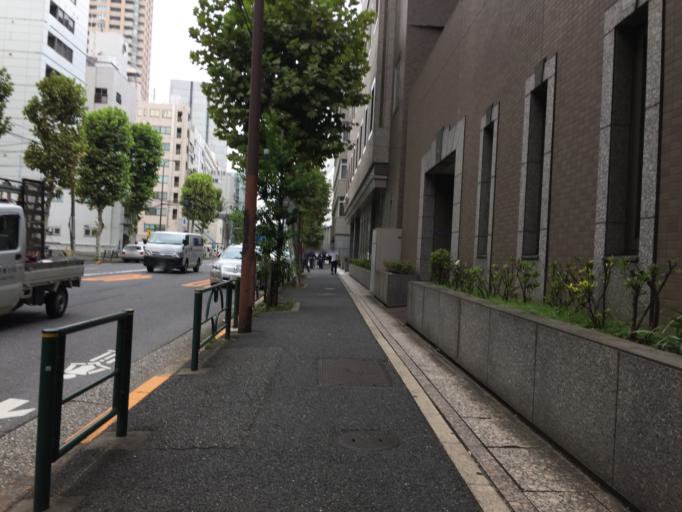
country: JP
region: Tokyo
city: Tokyo
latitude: 35.6697
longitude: 139.7268
